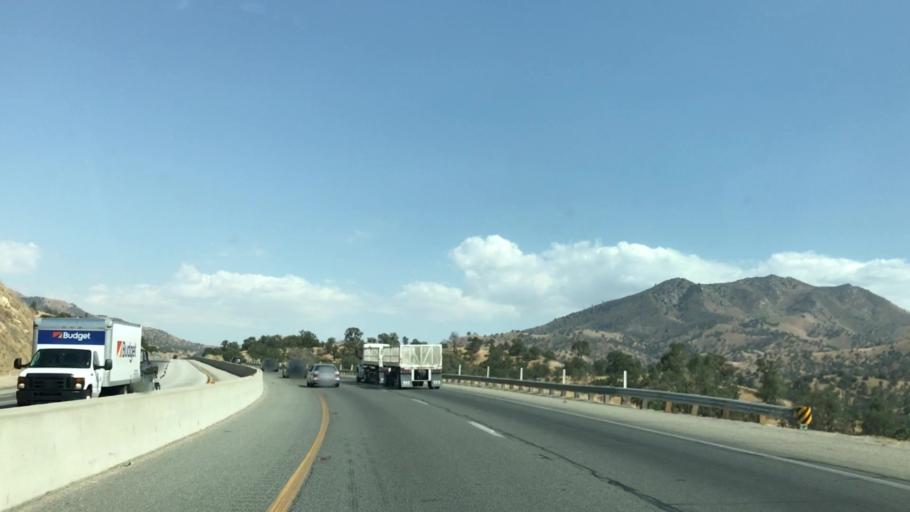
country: US
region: California
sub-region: Kern County
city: Golden Hills
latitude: 35.2152
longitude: -118.5514
